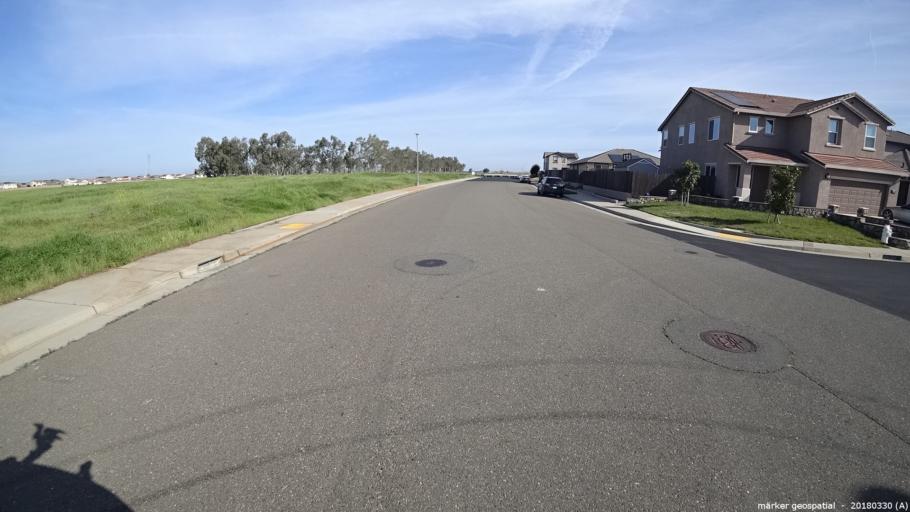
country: US
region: California
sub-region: Sacramento County
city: Vineyard
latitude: 38.4877
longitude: -121.3437
